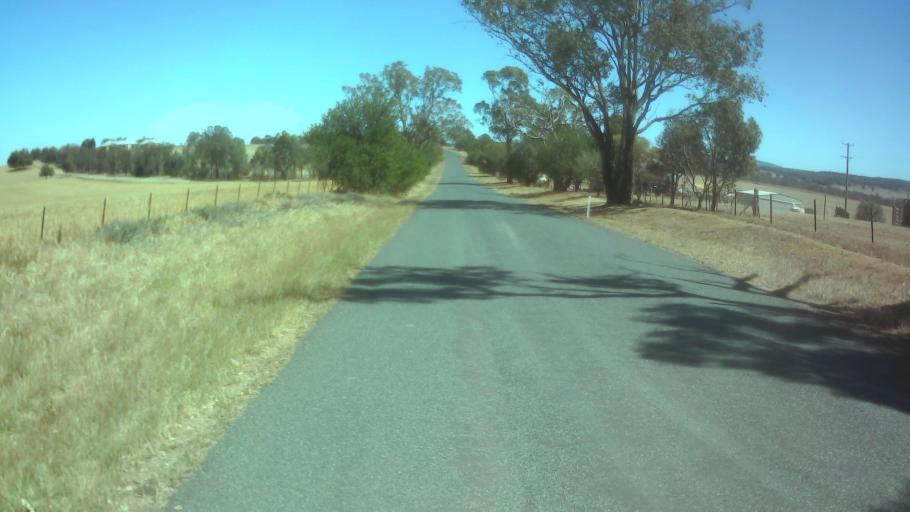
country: AU
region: New South Wales
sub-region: Weddin
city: Grenfell
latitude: -33.9497
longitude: 148.3956
